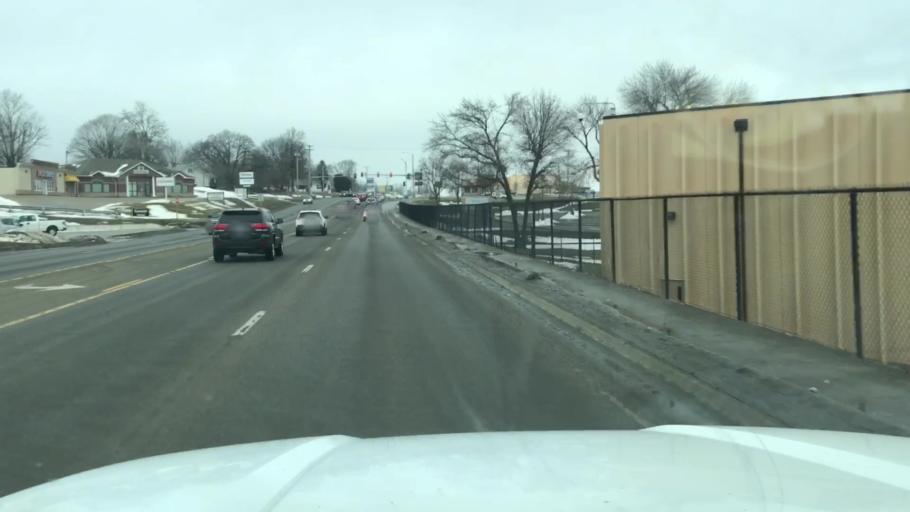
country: US
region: Missouri
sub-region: Andrew County
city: Country Club Village
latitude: 39.7905
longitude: -94.8087
